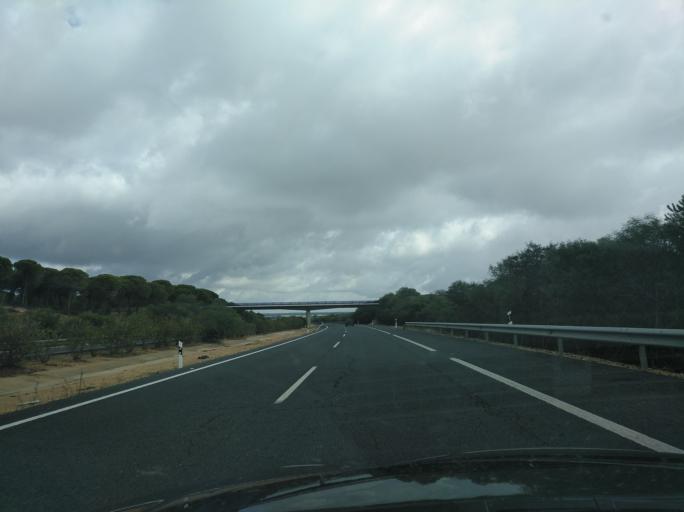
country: ES
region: Andalusia
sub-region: Provincia de Huelva
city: Cartaya
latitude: 37.3212
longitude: -7.1791
